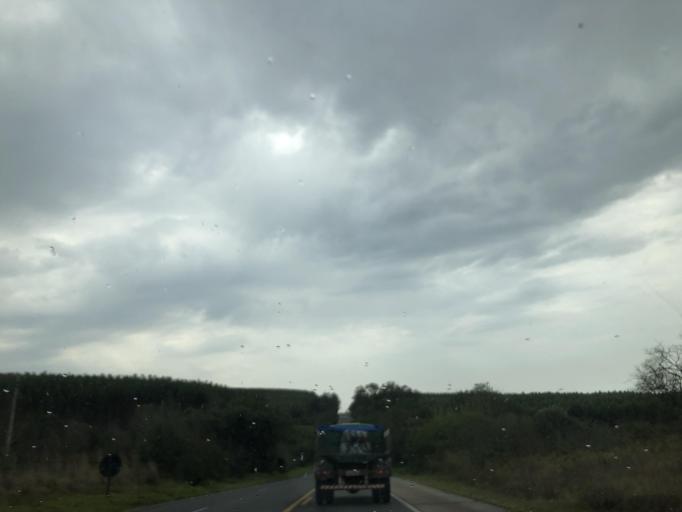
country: BR
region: Sao Paulo
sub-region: Salto De Pirapora
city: Salto de Pirapora
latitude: -23.6804
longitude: -47.6049
